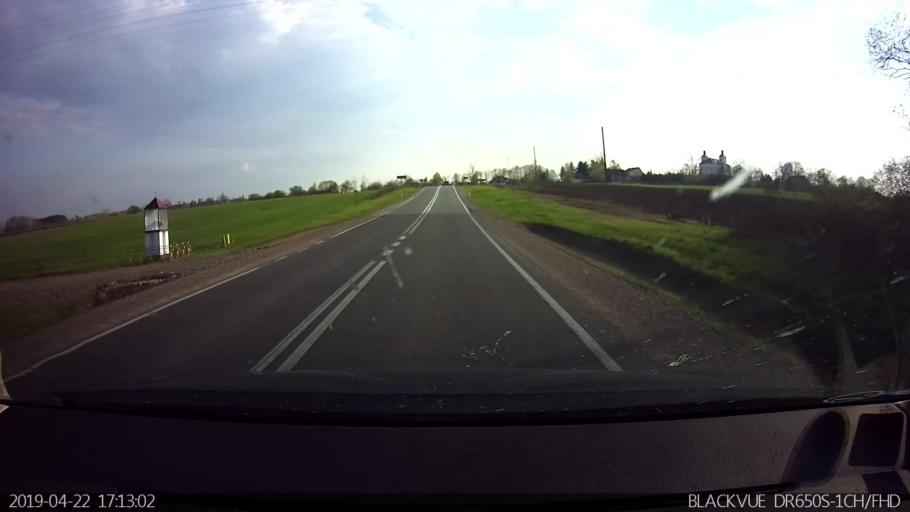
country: PL
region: Masovian Voivodeship
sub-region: Powiat siedlecki
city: Korczew
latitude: 52.4034
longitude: 22.5207
